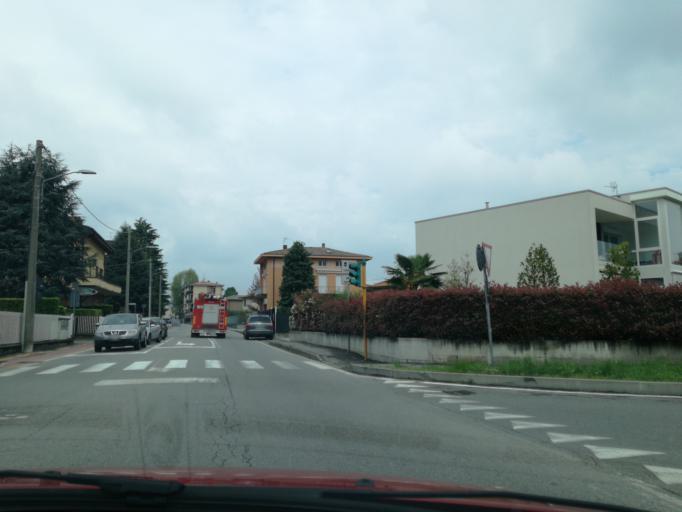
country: IT
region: Lombardy
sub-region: Provincia di Lecco
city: Merate
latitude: 45.6952
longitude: 9.4127
